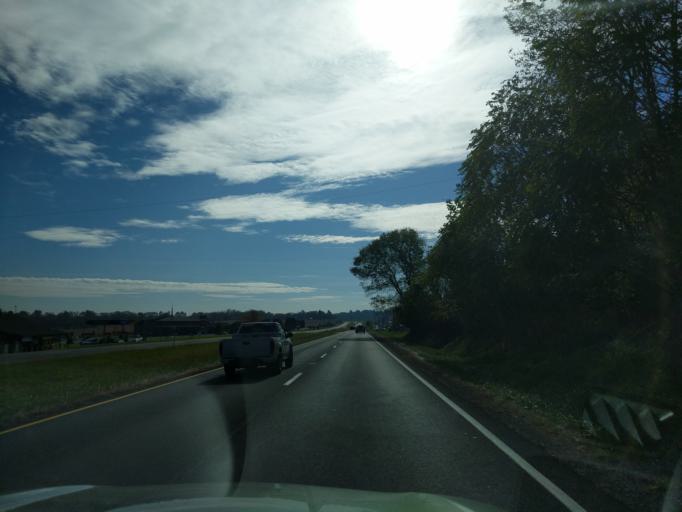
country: US
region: Virginia
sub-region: City of Winchester
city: Winchester
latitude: 39.2229
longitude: -78.1973
